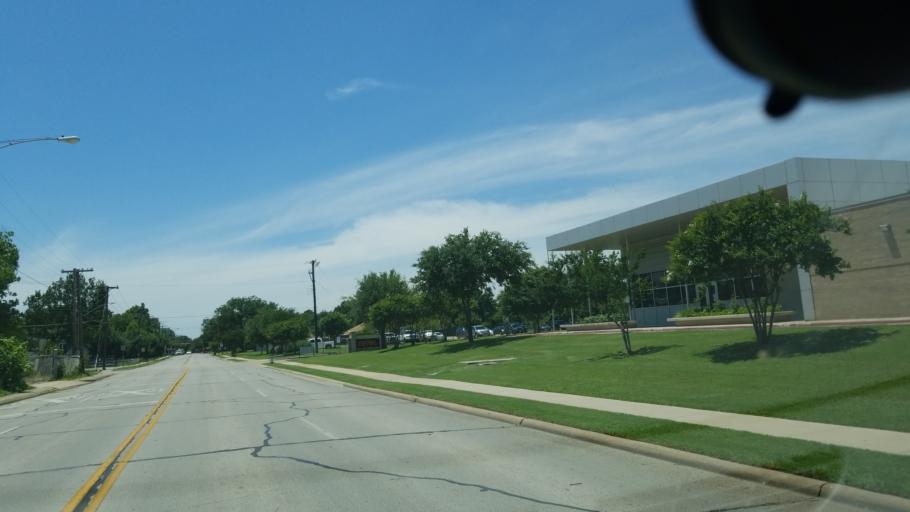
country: US
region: Texas
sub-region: Dallas County
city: Irving
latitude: 32.8212
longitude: -96.9454
